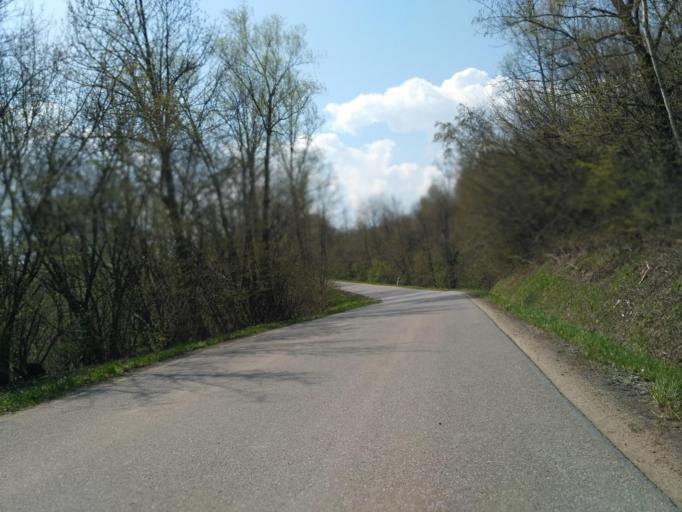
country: PL
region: Subcarpathian Voivodeship
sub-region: Powiat sanocki
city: Zarszyn
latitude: 49.5542
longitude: 21.9902
